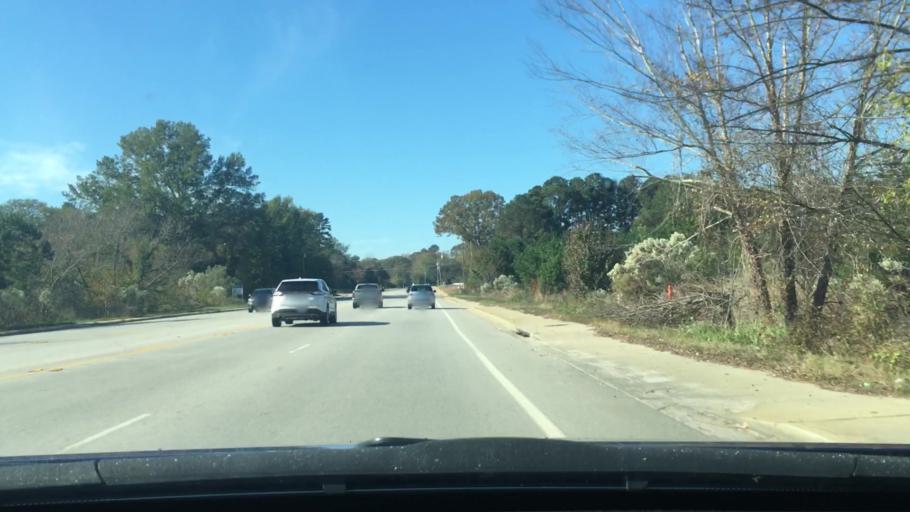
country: US
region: South Carolina
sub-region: Sumter County
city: South Sumter
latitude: 33.9039
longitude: -80.3821
